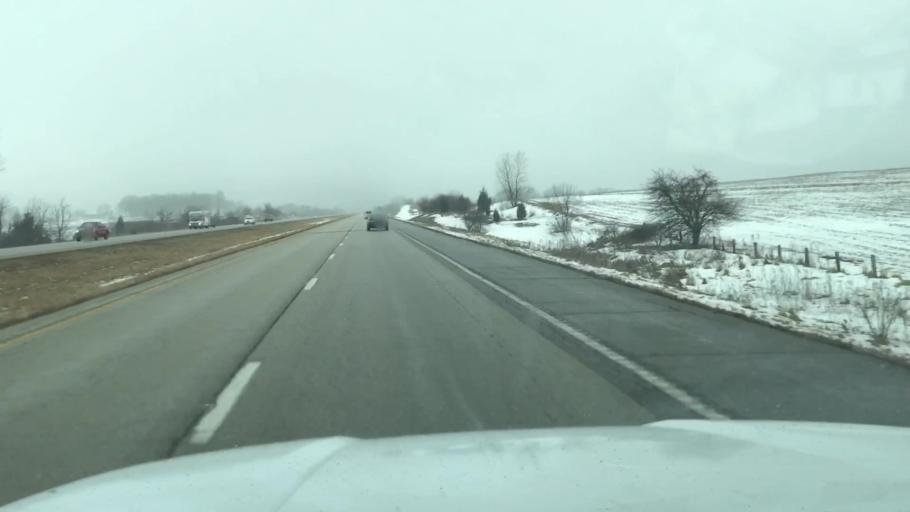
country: US
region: Missouri
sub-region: Andrew County
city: Country Club Village
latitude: 39.7478
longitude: -94.6875
